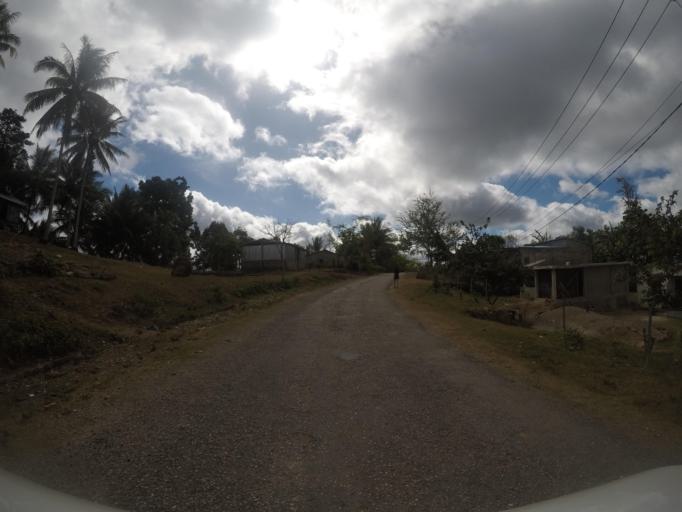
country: TL
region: Lautem
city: Lospalos
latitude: -8.5349
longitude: 126.9356
